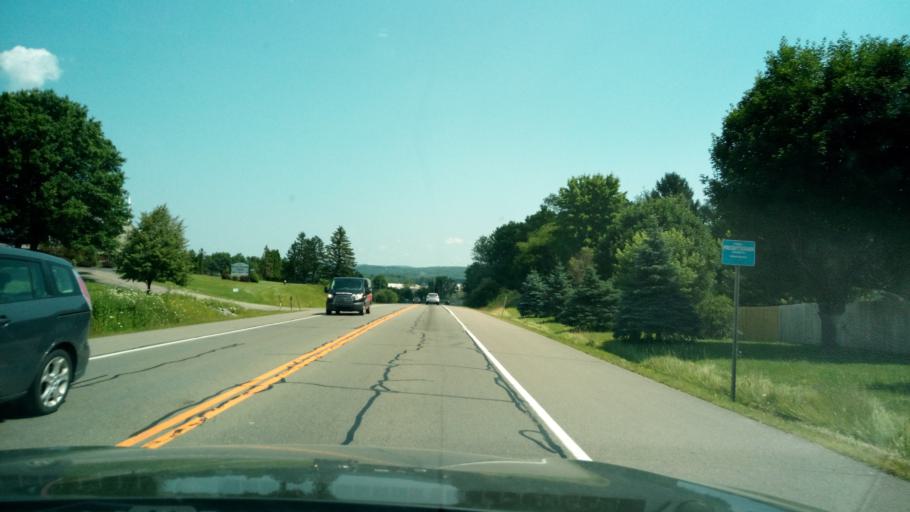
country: US
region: New York
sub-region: Chemung County
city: Horseheads
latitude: 42.1787
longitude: -76.8351
